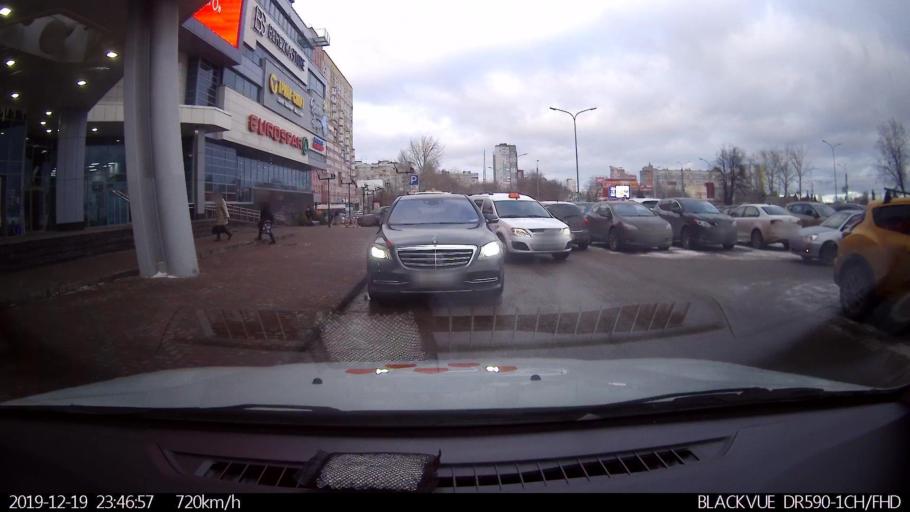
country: RU
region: Jaroslavl
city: Breytovo
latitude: 58.2545
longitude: 37.7654
